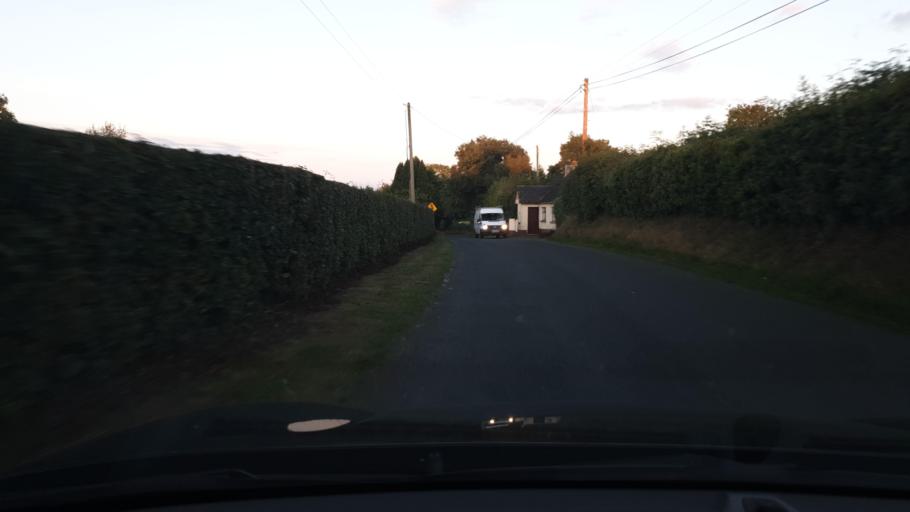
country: IE
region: Leinster
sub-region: Kildare
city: Prosperous
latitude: 53.3185
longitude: -6.8121
